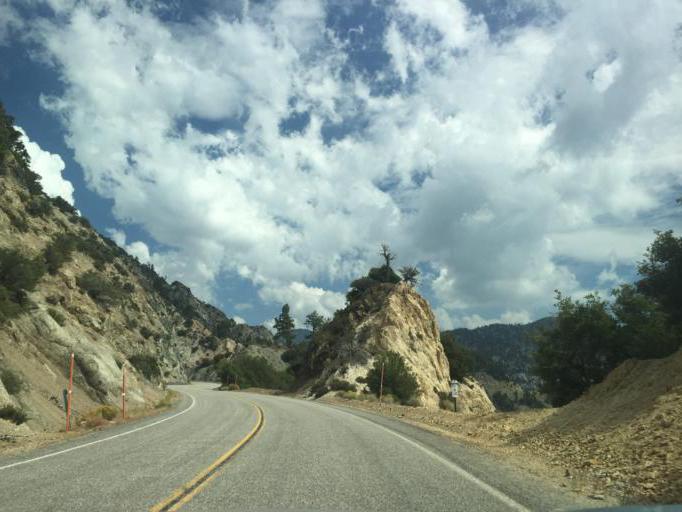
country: US
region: California
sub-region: Los Angeles County
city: Littlerock
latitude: 34.3616
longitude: -117.8691
